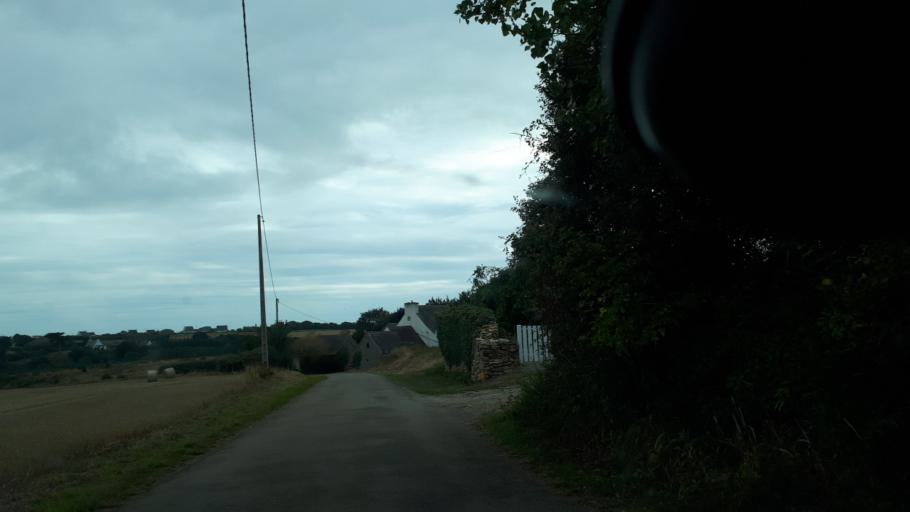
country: FR
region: Brittany
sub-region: Departement du Finistere
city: Plozevet
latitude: 47.9678
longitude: -4.3940
